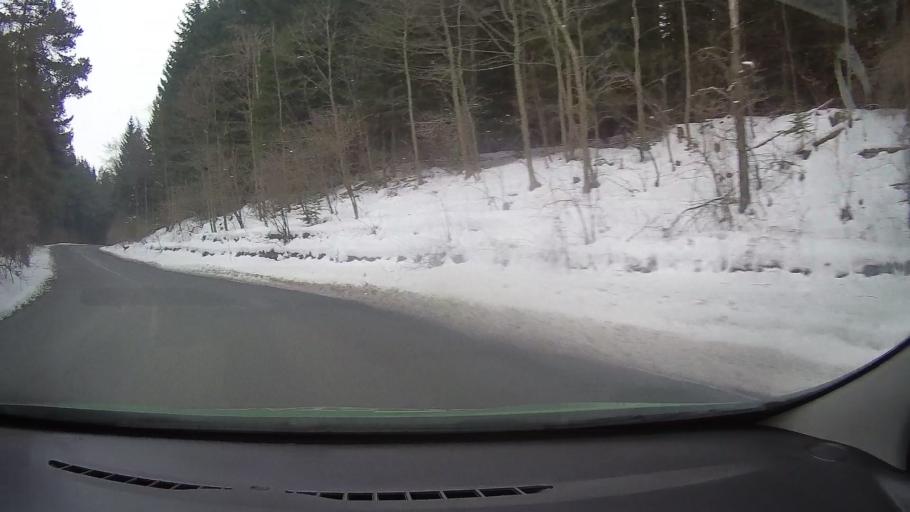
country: RO
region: Brasov
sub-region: Oras Predeal
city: Predeal
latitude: 45.5201
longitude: 25.5016
